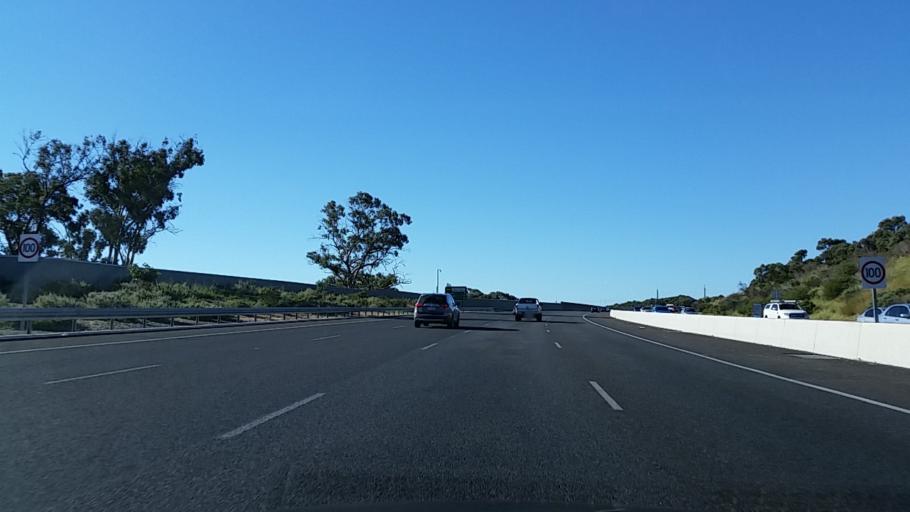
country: AU
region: South Australia
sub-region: Marion
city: Trott Park
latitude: -35.0749
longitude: 138.5436
